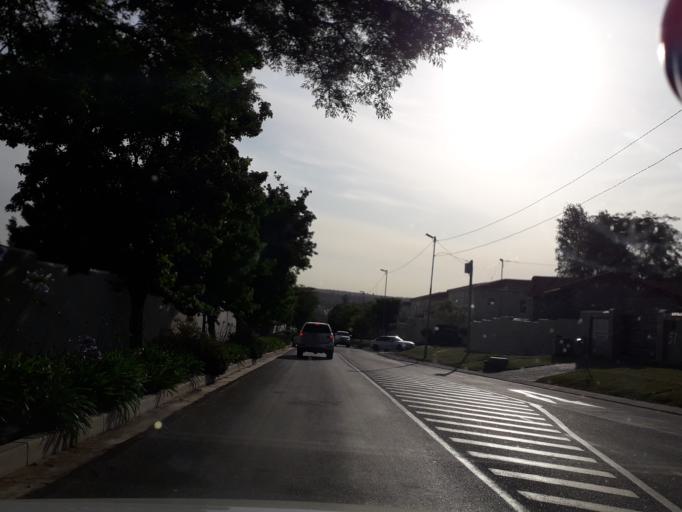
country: ZA
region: Gauteng
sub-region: City of Johannesburg Metropolitan Municipality
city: Diepsloot
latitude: -26.0437
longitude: 27.9959
